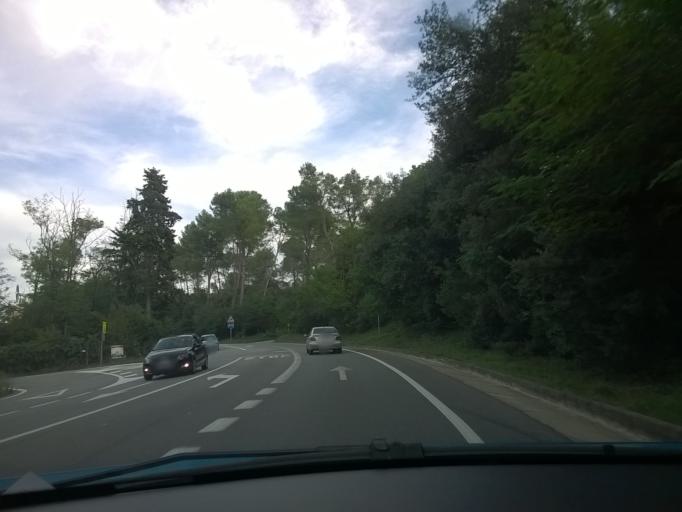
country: ES
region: Catalonia
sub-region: Provincia de Barcelona
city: Sant Cugat del Valles
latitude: 41.4578
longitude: 2.0897
